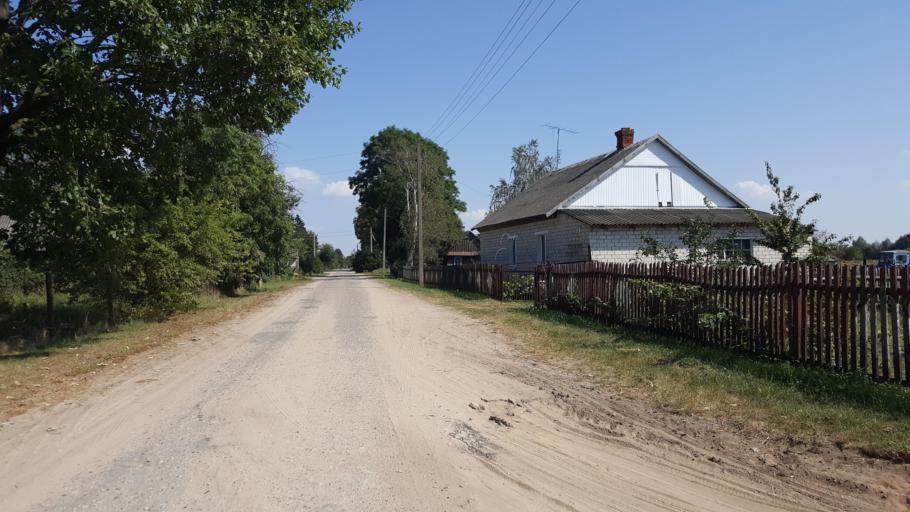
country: PL
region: Podlasie
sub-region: Powiat hajnowski
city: Czeremcha
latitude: 52.4790
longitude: 23.5366
